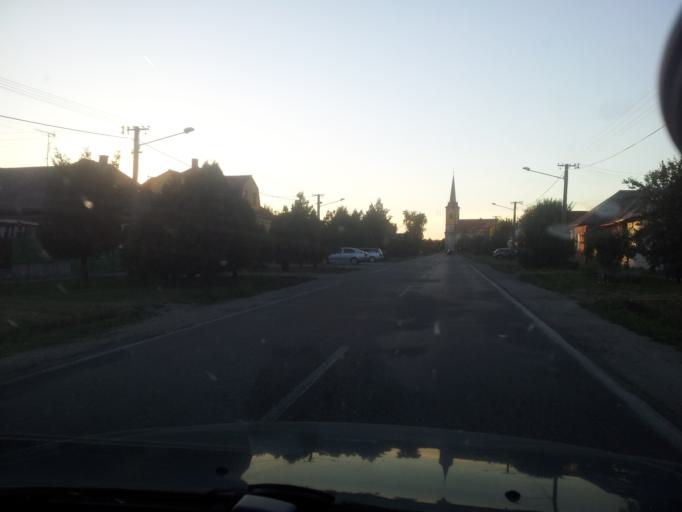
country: SK
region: Nitriansky
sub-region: Okres Nove Zamky
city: Sturovo
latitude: 47.8514
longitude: 18.6559
